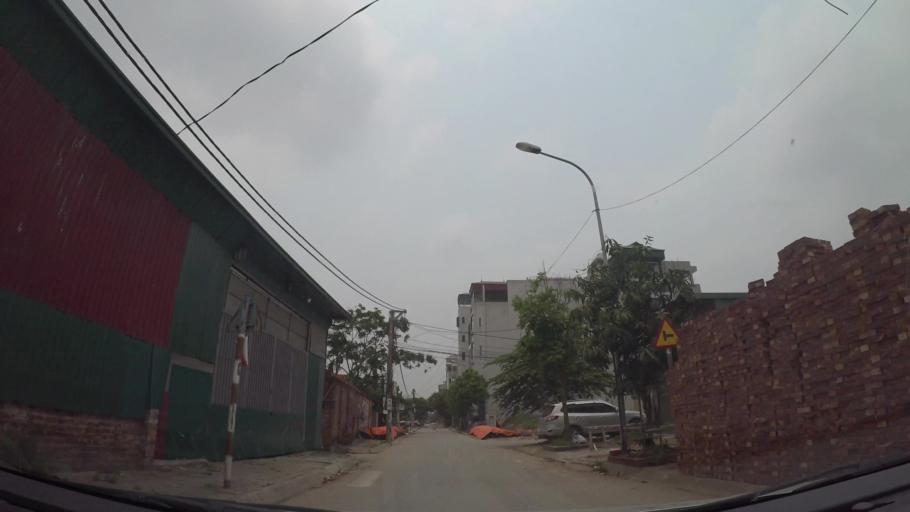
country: VN
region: Ha Noi
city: Ha Dong
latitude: 20.9886
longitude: 105.7433
